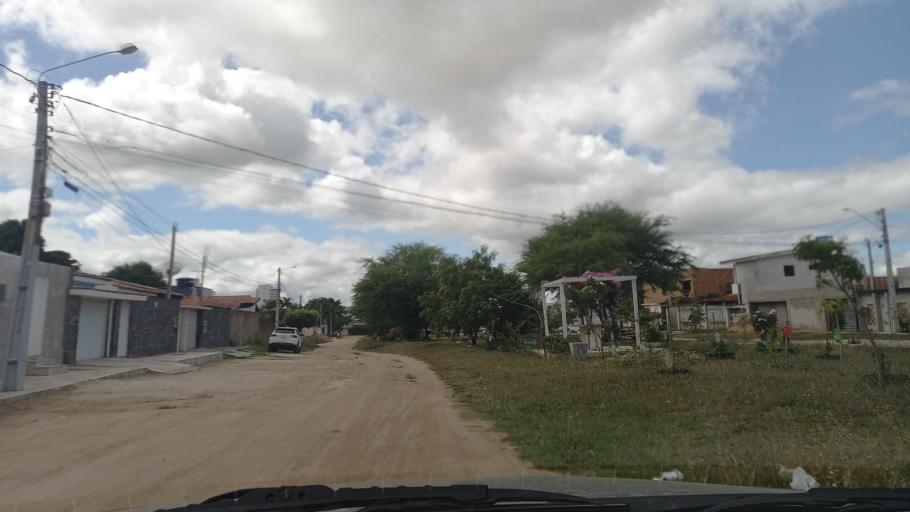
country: BR
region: Pernambuco
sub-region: Caruaru
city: Caruaru
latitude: -8.2597
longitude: -35.9789
